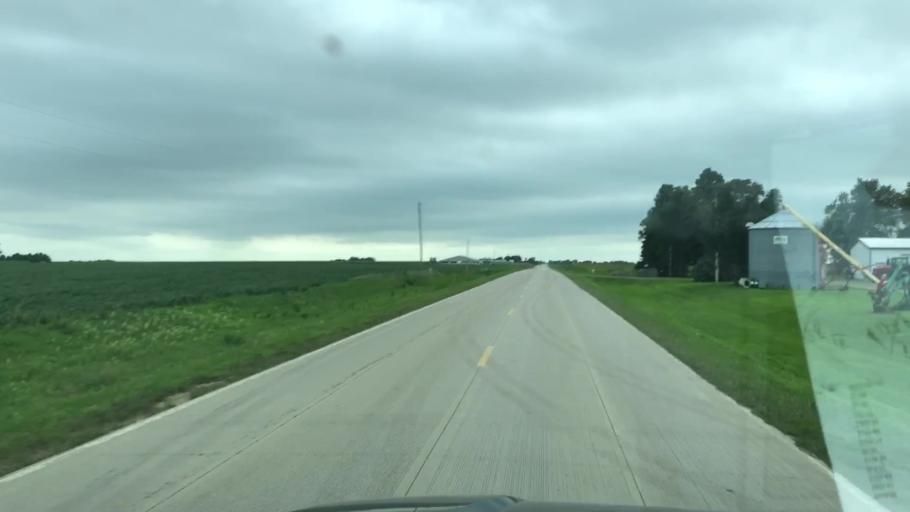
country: US
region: Iowa
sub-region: O'Brien County
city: Sheldon
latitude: 43.1332
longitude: -95.9792
